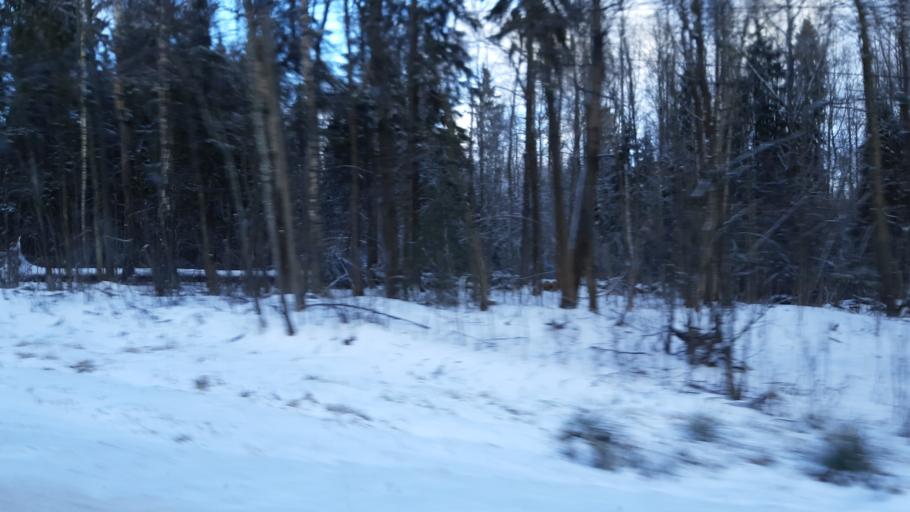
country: RU
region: Moskovskaya
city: Svatkovo
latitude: 56.3185
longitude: 38.3004
